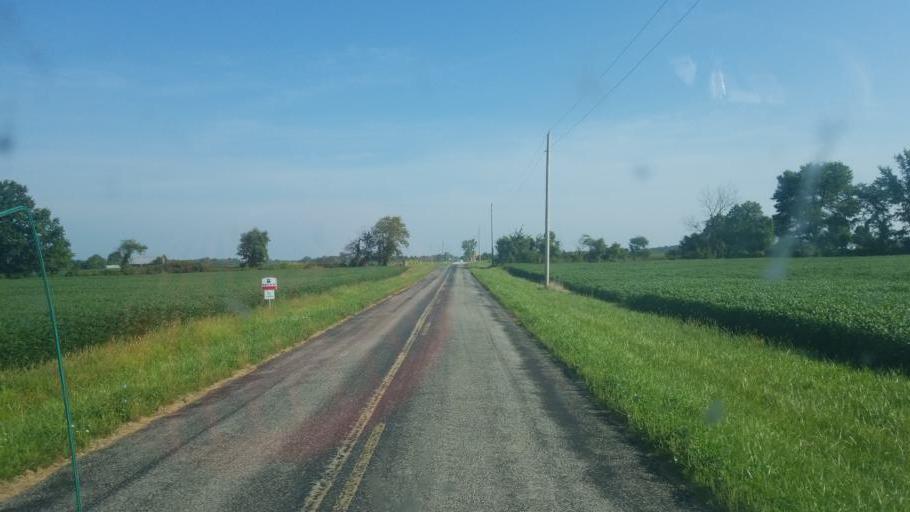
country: US
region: Ohio
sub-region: Huron County
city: New London
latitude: 41.0783
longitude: -82.3472
